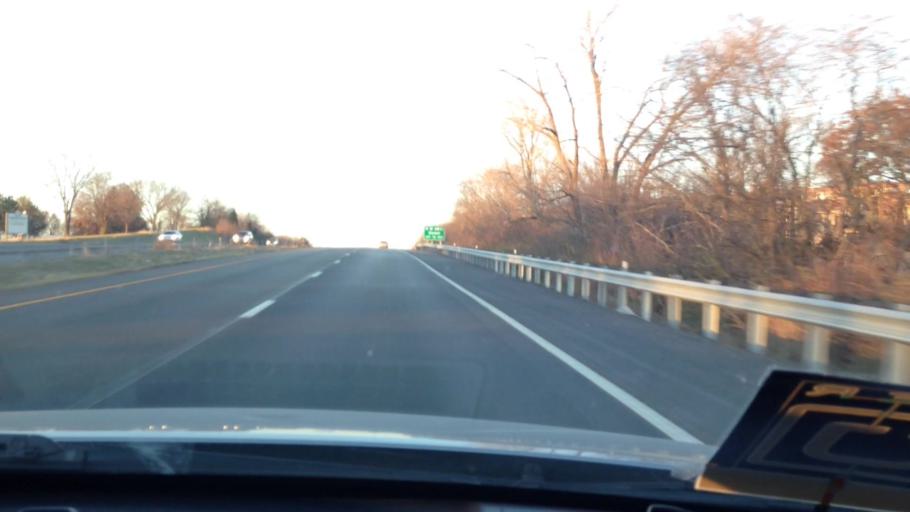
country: US
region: Missouri
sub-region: Clay County
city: Gladstone
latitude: 39.2045
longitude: -94.5896
